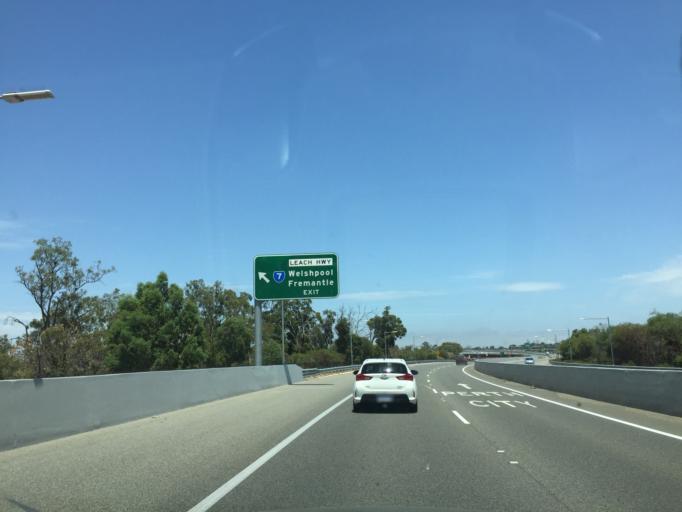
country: AU
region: Western Australia
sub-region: Belmont
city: Kewdale
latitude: -31.9634
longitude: 115.9631
